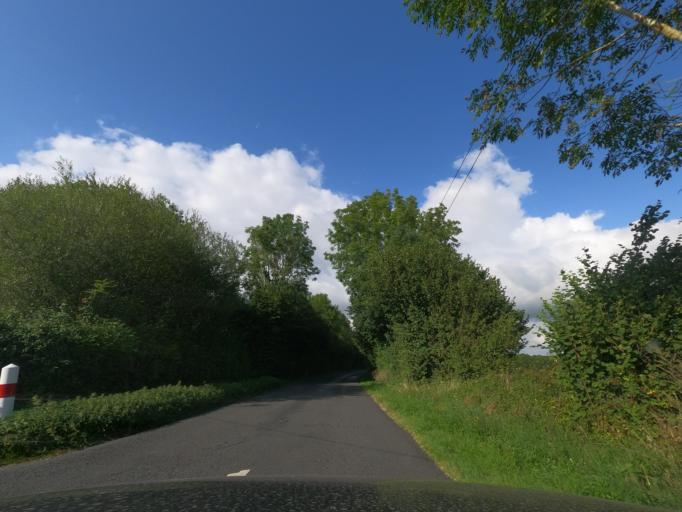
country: FR
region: Lower Normandy
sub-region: Departement de l'Orne
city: Gace
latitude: 48.7738
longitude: 0.2567
